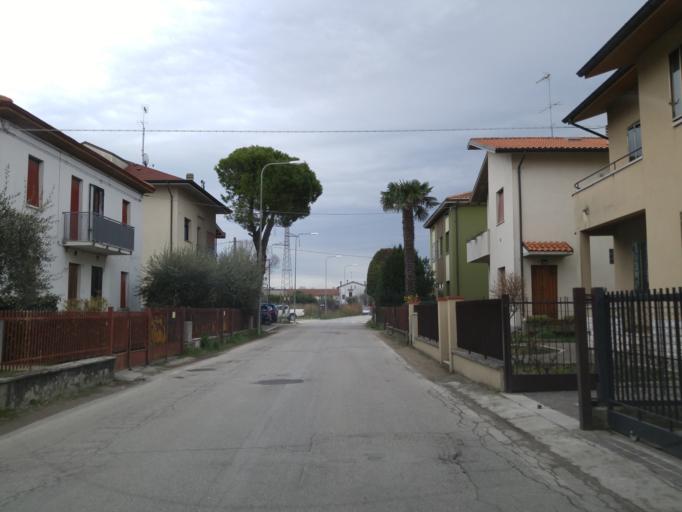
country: IT
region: The Marches
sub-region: Provincia di Pesaro e Urbino
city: Centinarola
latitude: 43.8399
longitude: 12.9981
